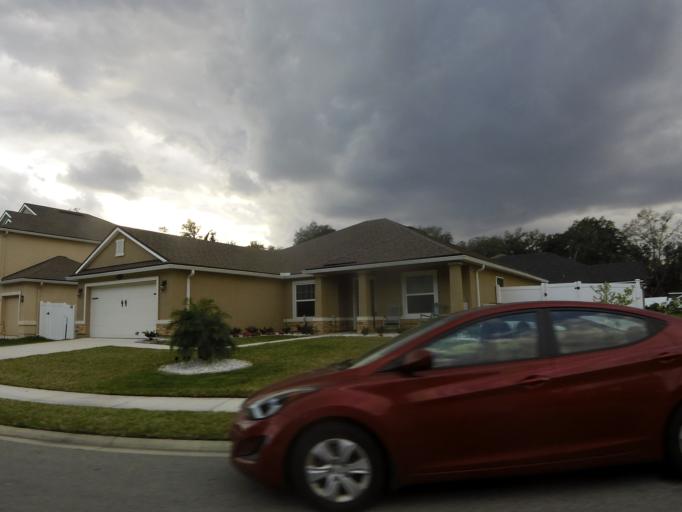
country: US
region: Florida
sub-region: Saint Johns County
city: Fruit Cove
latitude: 30.1756
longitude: -81.5660
